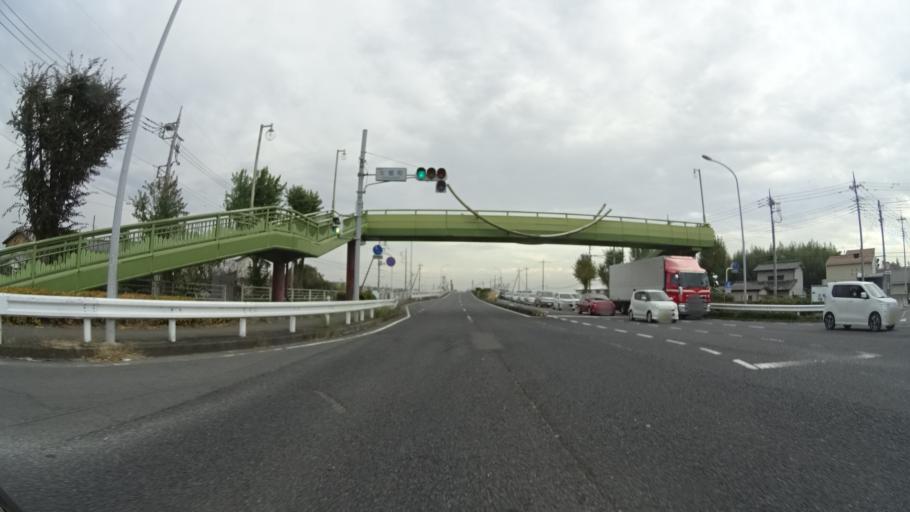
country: JP
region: Gunma
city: Maebashi-shi
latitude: 36.3731
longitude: 139.1291
